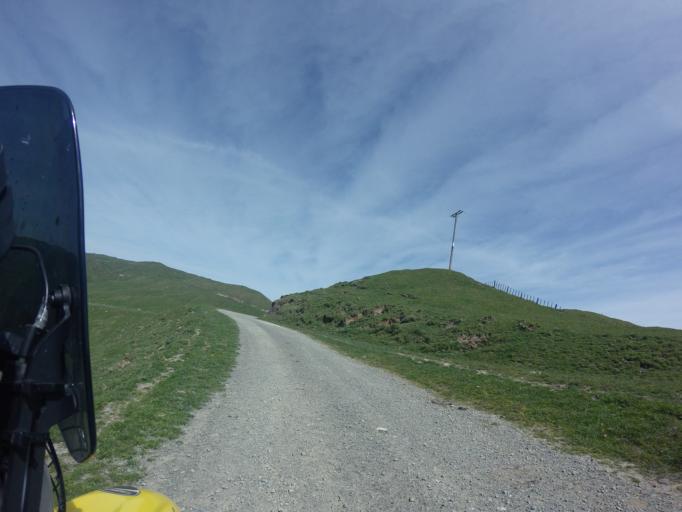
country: NZ
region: Bay of Plenty
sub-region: Opotiki District
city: Opotiki
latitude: -38.4533
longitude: 177.3613
